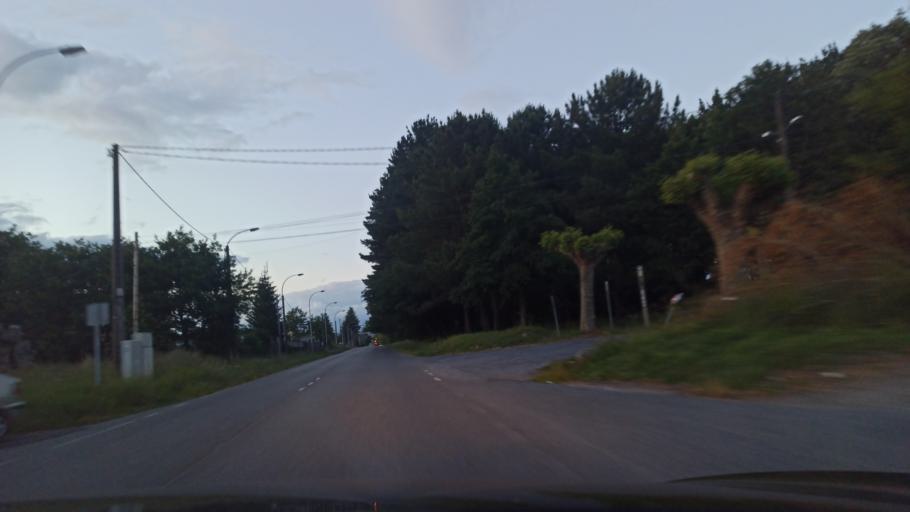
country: ES
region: Galicia
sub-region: Provincia de Lugo
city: Lugo
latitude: 42.9857
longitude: -7.5819
